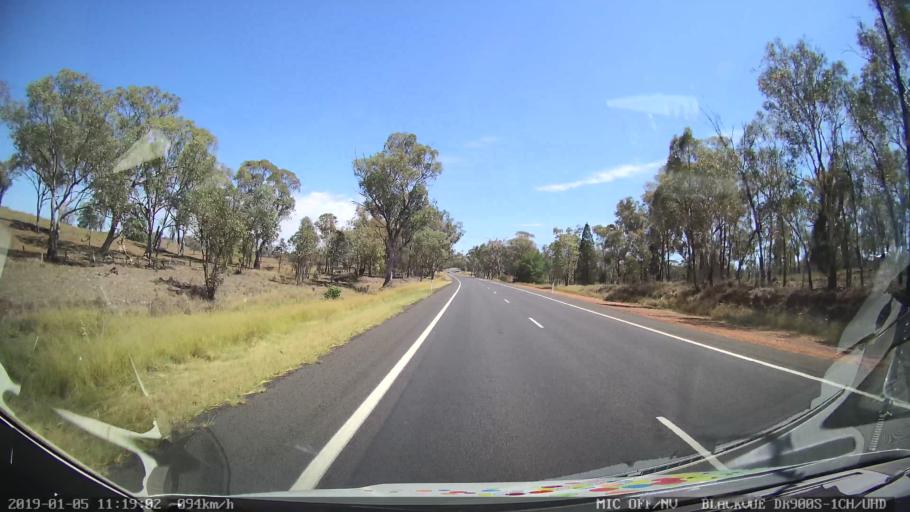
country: AU
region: New South Wales
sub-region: Warrumbungle Shire
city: Coonabarabran
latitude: -31.3091
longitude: 149.2977
